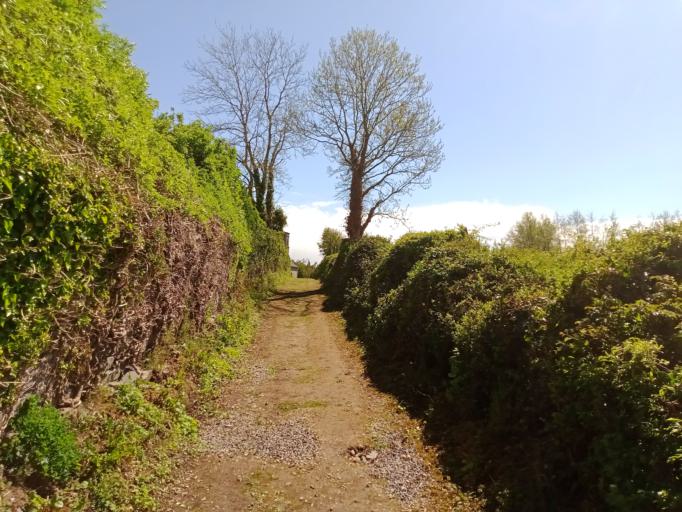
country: IE
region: Leinster
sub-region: Kilkenny
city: Kilkenny
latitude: 52.6902
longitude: -7.2595
